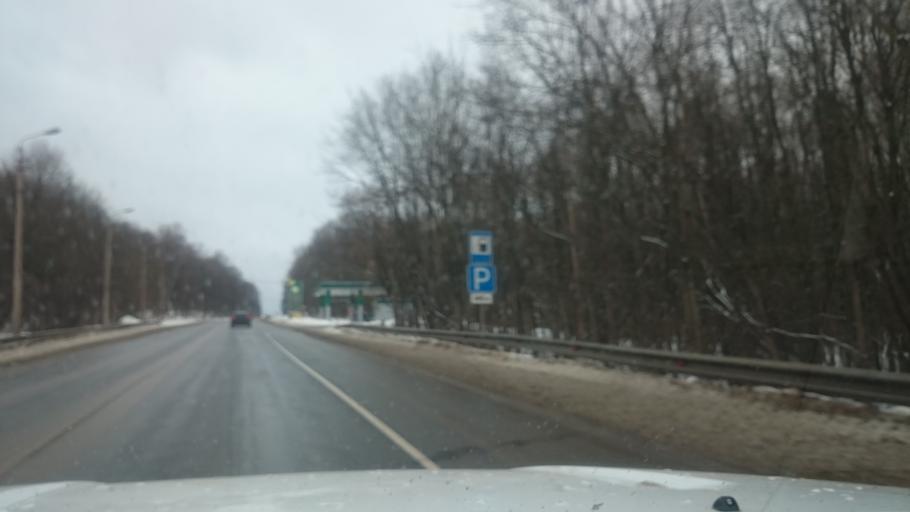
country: RU
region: Tula
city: Kosaya Gora
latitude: 54.0964
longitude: 37.5494
